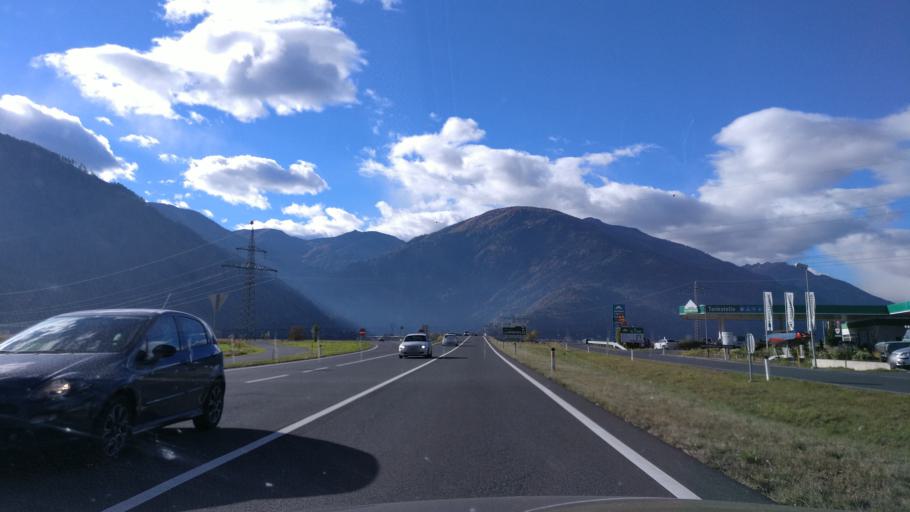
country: AT
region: Carinthia
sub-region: Politischer Bezirk Spittal an der Drau
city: Lendorf
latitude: 46.8329
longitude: 13.4054
